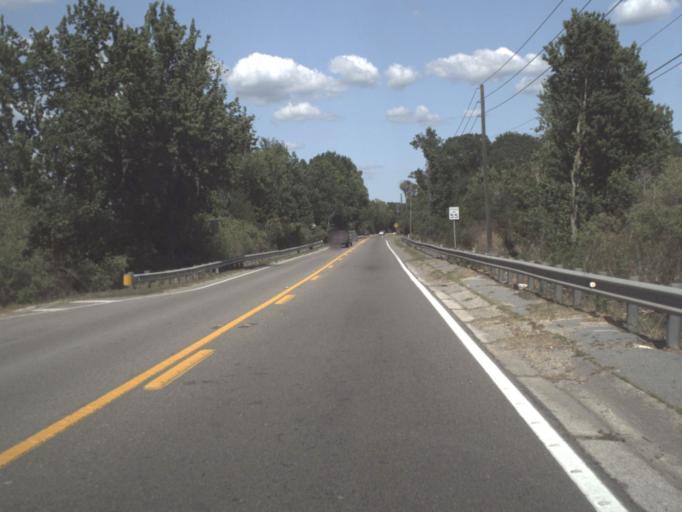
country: US
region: Florida
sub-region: Lake County
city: Mount Dora
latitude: 28.7977
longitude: -81.6209
